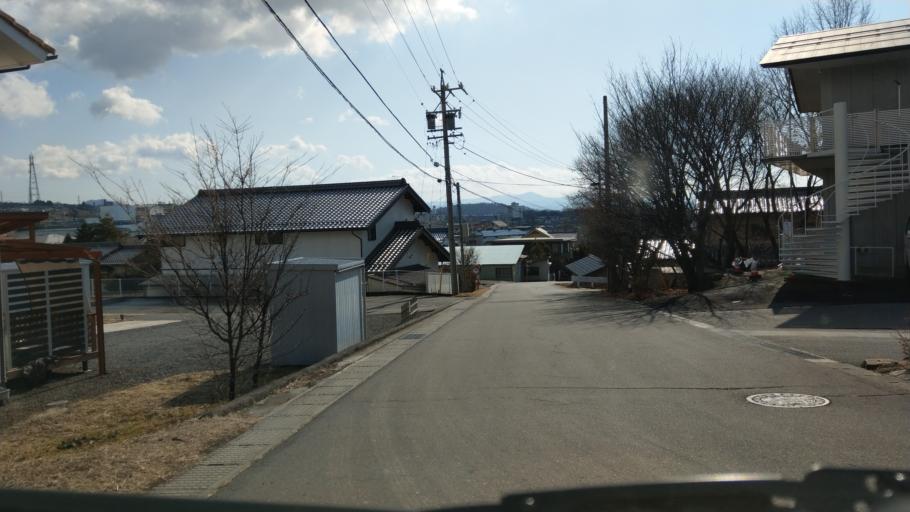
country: JP
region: Nagano
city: Komoro
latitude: 36.3392
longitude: 138.4126
